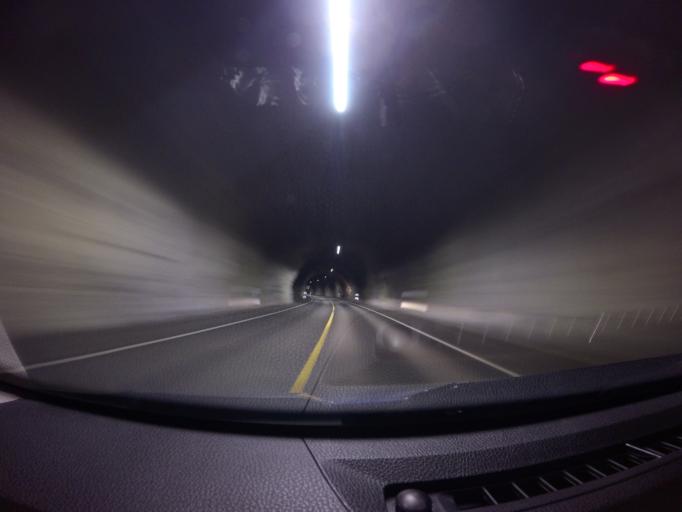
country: NO
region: Rogaland
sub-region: Forsand
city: Forsand
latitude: 58.8080
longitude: 6.2631
